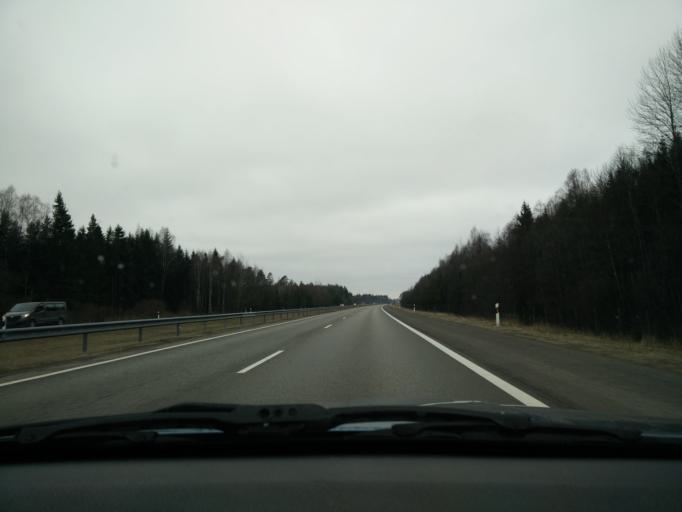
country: LT
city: Rietavas
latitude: 55.6159
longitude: 22.0110
